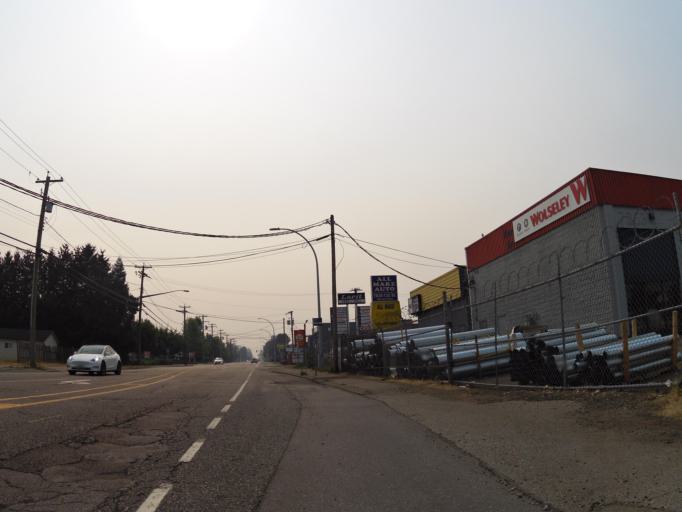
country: CA
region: British Columbia
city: Delta
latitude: 49.1455
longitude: -122.8568
